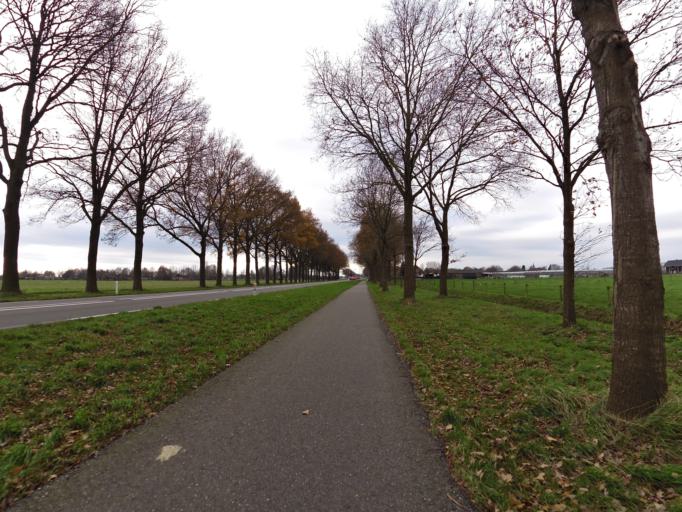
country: NL
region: Gelderland
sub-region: Gemeente Doesburg
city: Doesburg
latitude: 51.9535
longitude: 6.1564
